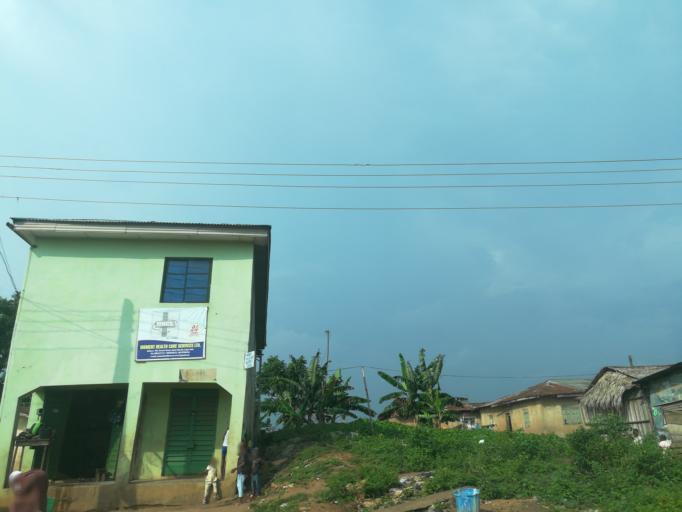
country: NG
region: Lagos
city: Ikorodu
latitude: 6.6632
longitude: 3.6672
